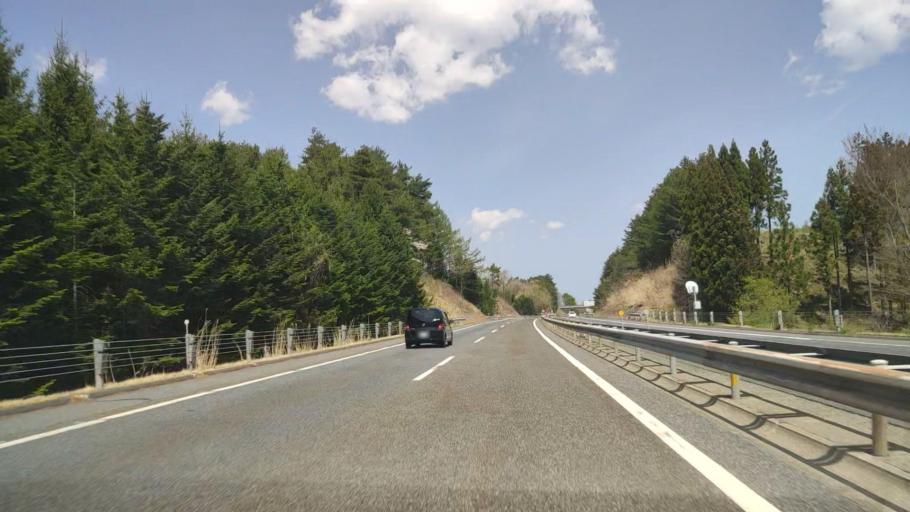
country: JP
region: Aomori
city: Hachinohe
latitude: 40.3441
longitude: 141.4492
